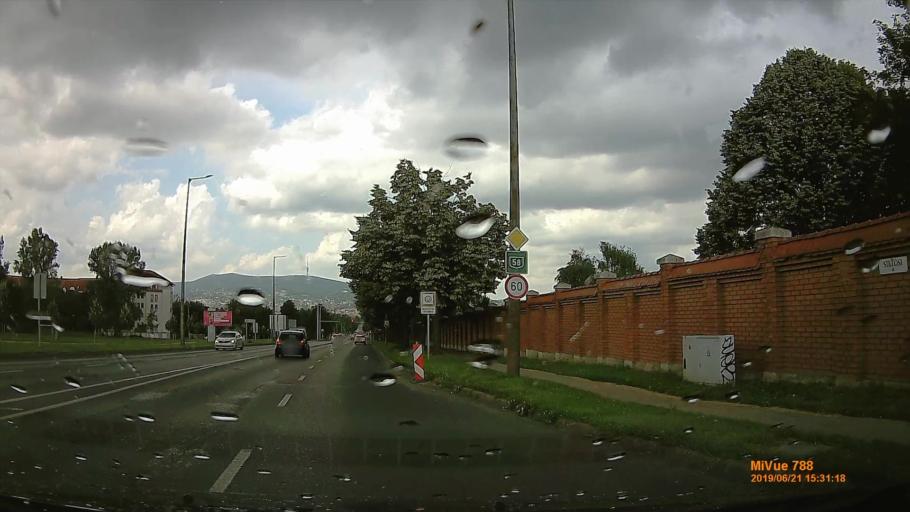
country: HU
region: Baranya
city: Pecs
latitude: 46.0457
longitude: 18.2319
